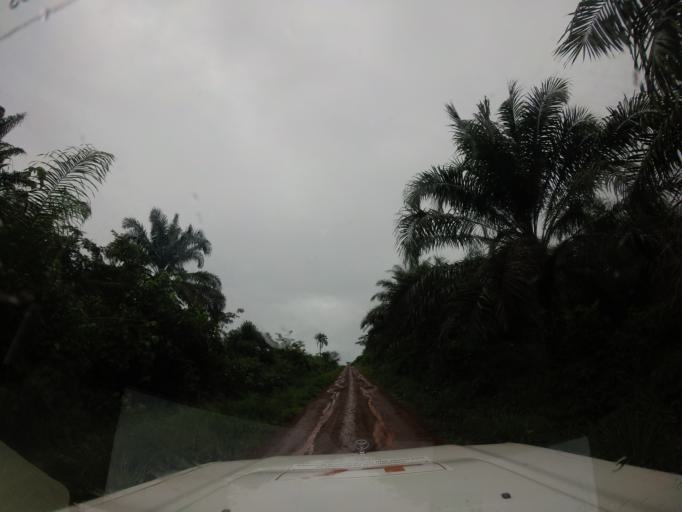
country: SL
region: Eastern Province
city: Kenema
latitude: 7.7447
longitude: -11.1929
